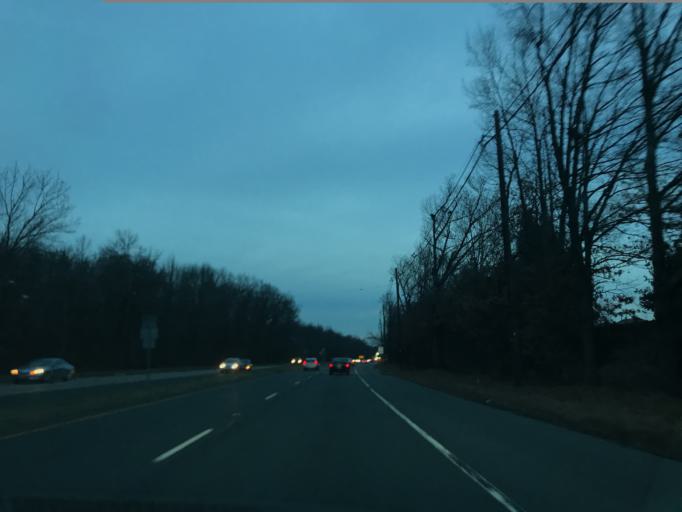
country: US
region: New Jersey
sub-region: Middlesex County
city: Cranbury
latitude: 40.3004
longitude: -74.5130
